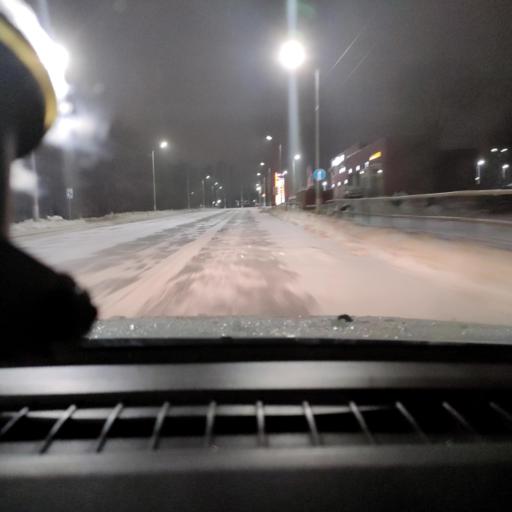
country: RU
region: Samara
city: Novokuybyshevsk
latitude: 53.0881
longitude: 49.9454
